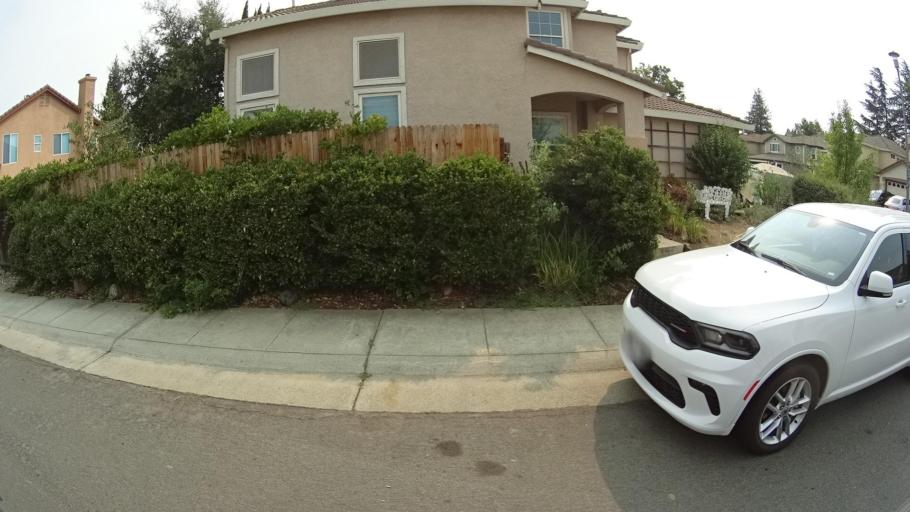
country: US
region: California
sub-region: Sacramento County
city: Laguna
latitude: 38.4140
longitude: -121.4009
